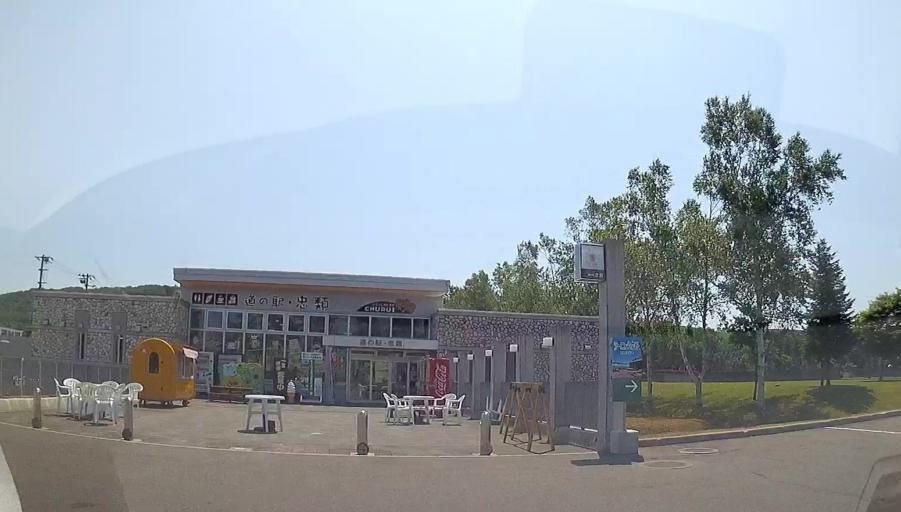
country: JP
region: Hokkaido
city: Obihiro
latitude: 42.5591
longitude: 143.2988
